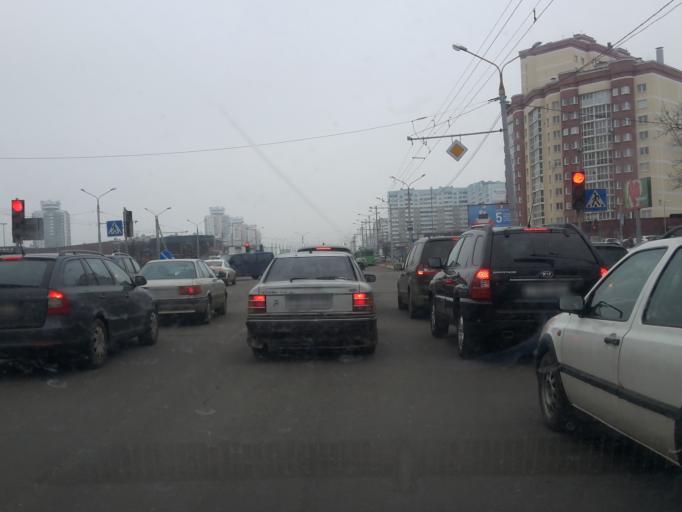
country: BY
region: Minsk
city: Novoye Medvezhino
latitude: 53.9044
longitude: 27.4357
